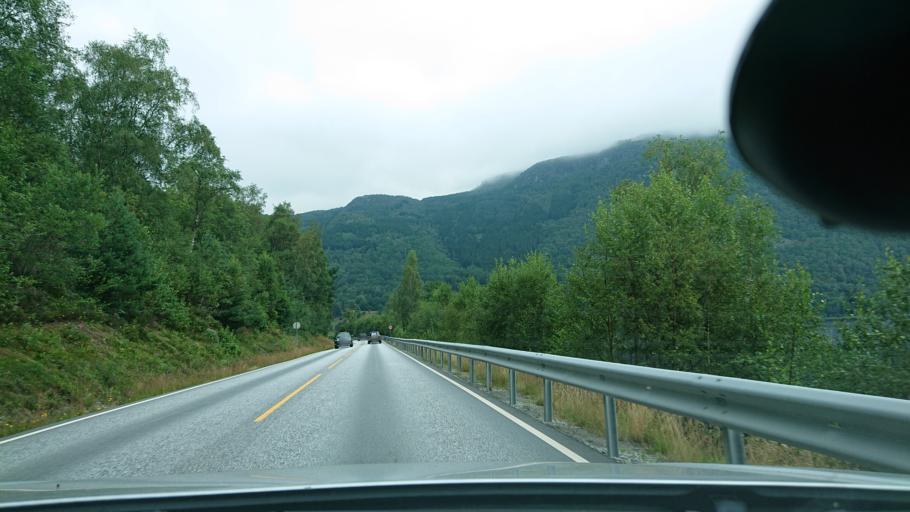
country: NO
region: Rogaland
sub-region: Hjelmeland
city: Hjelmelandsvagen
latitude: 59.1579
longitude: 6.1744
